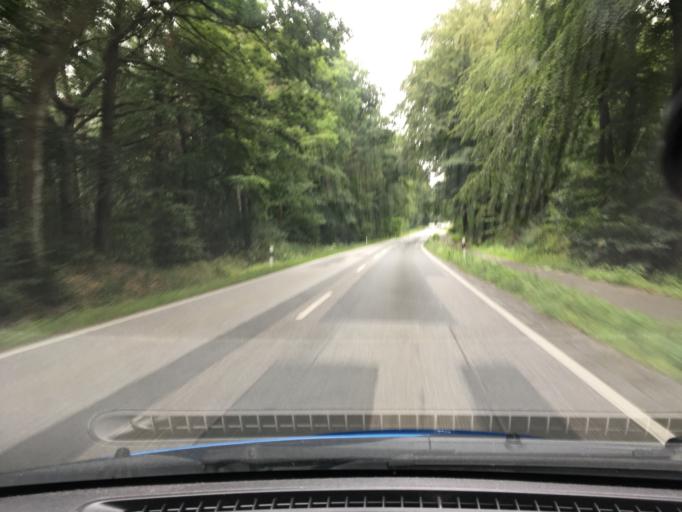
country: DE
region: Schleswig-Holstein
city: Schnakenbek
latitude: 53.3790
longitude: 10.5136
